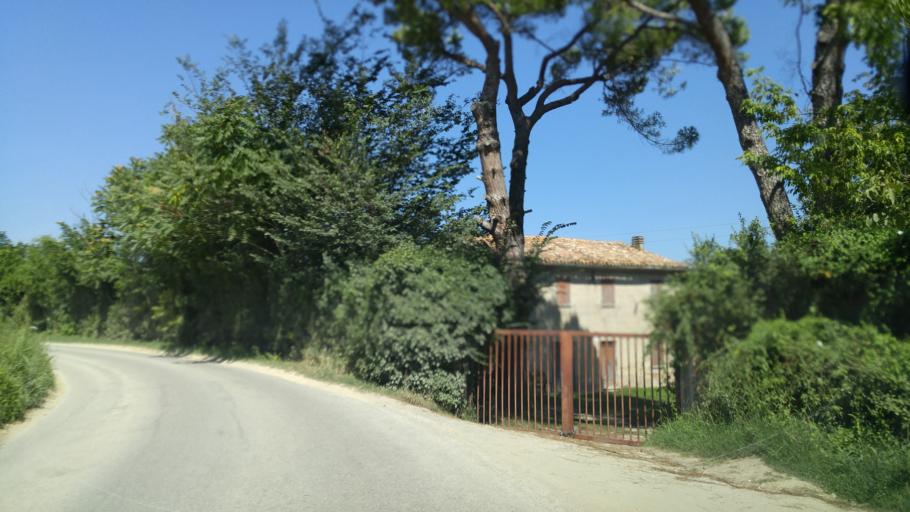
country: IT
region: The Marches
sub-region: Provincia di Pesaro e Urbino
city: Fenile
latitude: 43.8334
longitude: 12.9759
